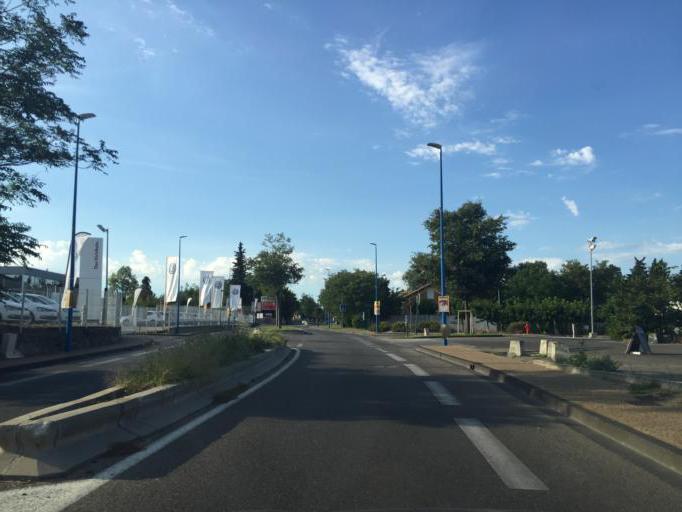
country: FR
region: Provence-Alpes-Cote d'Azur
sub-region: Departement du Vaucluse
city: Carpentras
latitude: 44.0392
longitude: 5.0498
